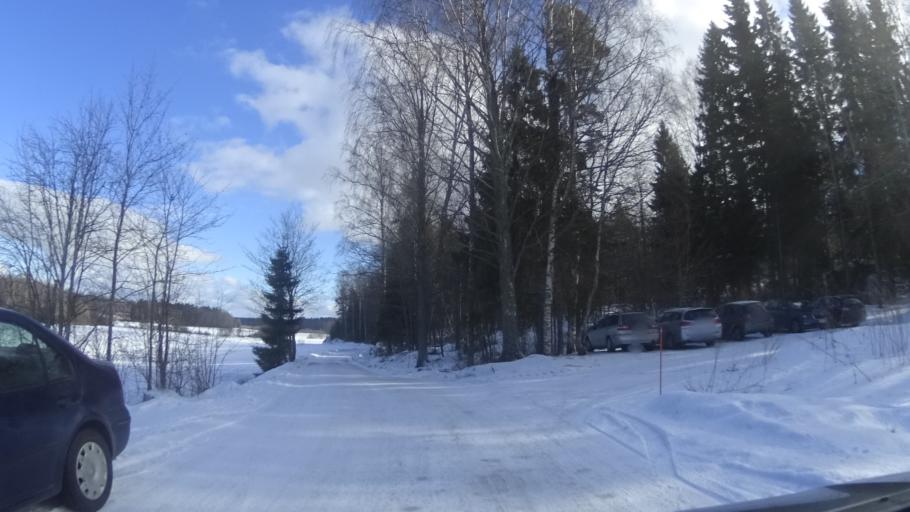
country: FI
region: Uusimaa
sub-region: Helsinki
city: Vantaa
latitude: 60.2486
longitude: 25.1650
